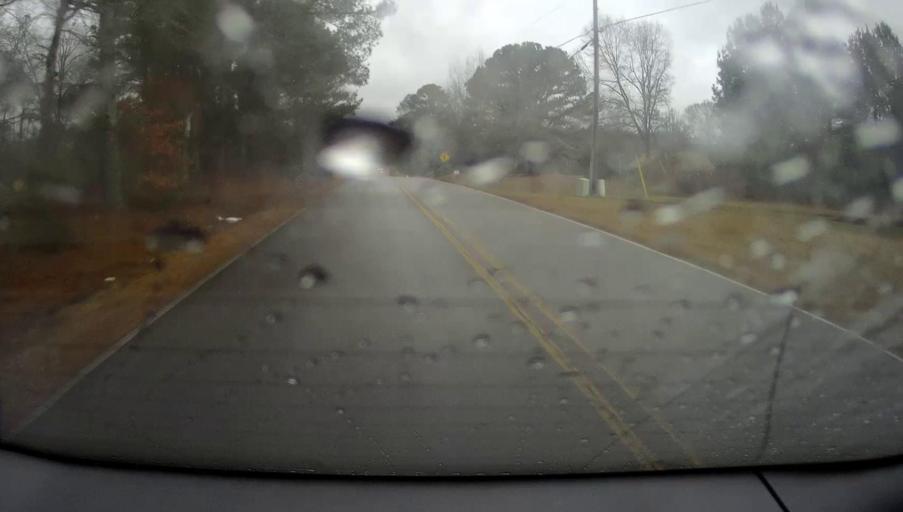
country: US
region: Alabama
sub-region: Morgan County
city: Hartselle
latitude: 34.4125
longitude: -86.9041
